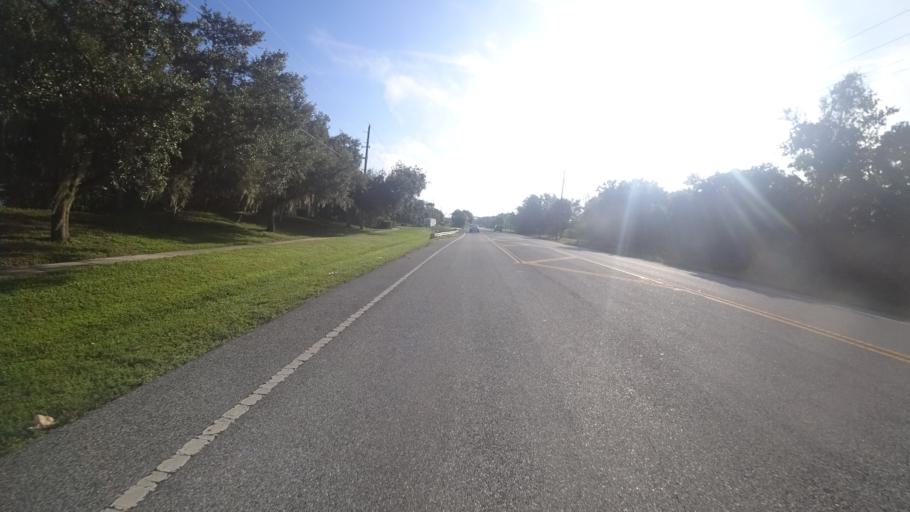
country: US
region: Florida
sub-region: Manatee County
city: Ellenton
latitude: 27.5426
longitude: -82.4628
